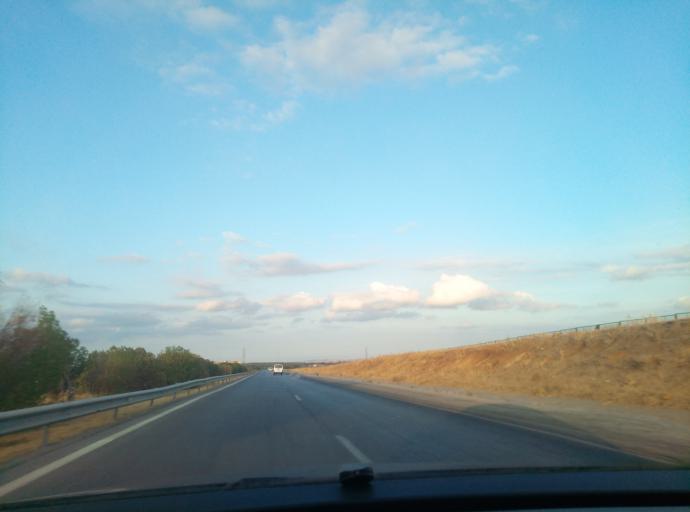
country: TN
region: Manouba
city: El Battan
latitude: 36.6627
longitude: 9.8506
